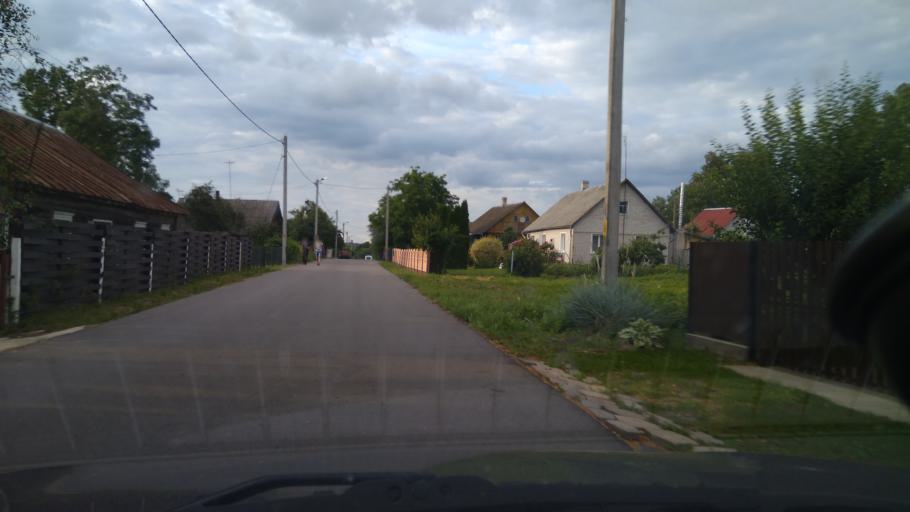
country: BY
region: Grodnenskaya
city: Shchuchin
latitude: 53.5348
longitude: 24.7291
